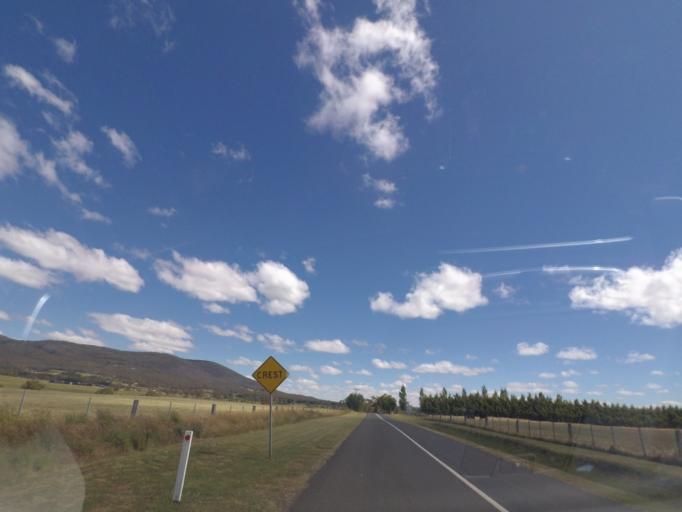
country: AU
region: Victoria
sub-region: Hume
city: Sunbury
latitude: -37.3368
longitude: 144.5579
